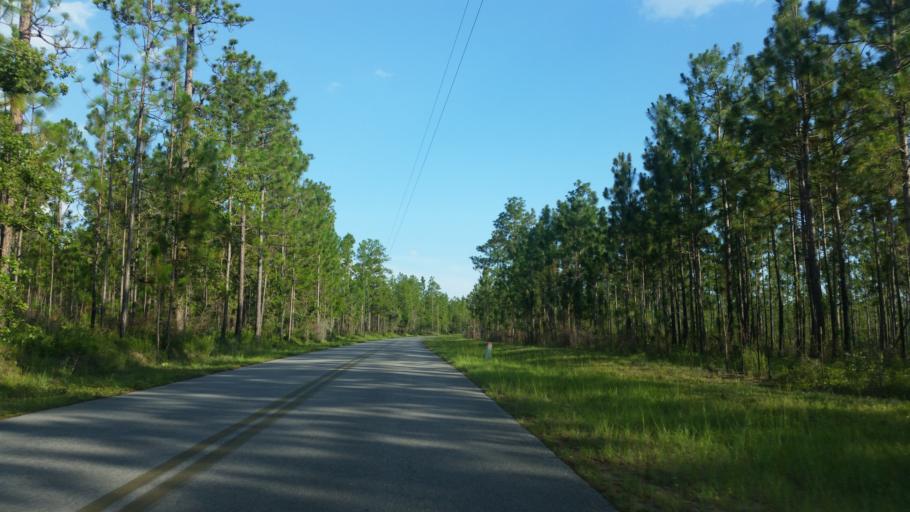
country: US
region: Florida
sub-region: Santa Rosa County
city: East Milton
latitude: 30.6982
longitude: -86.8757
